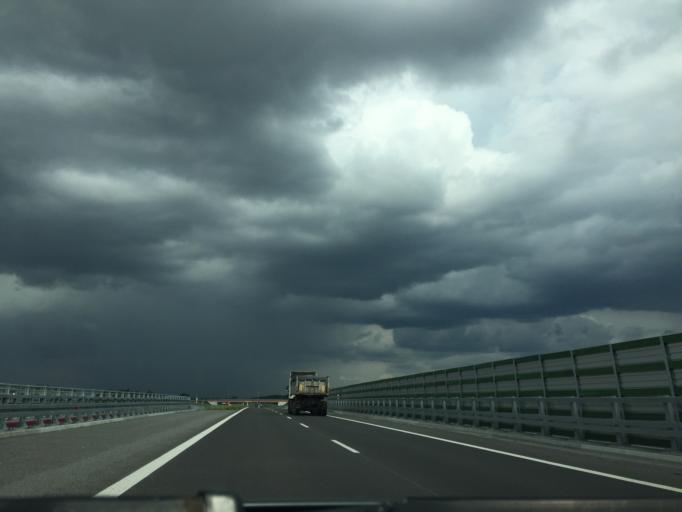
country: PL
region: Masovian Voivodeship
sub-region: Powiat szydlowiecki
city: Jastrzab
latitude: 51.2759
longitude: 20.9538
